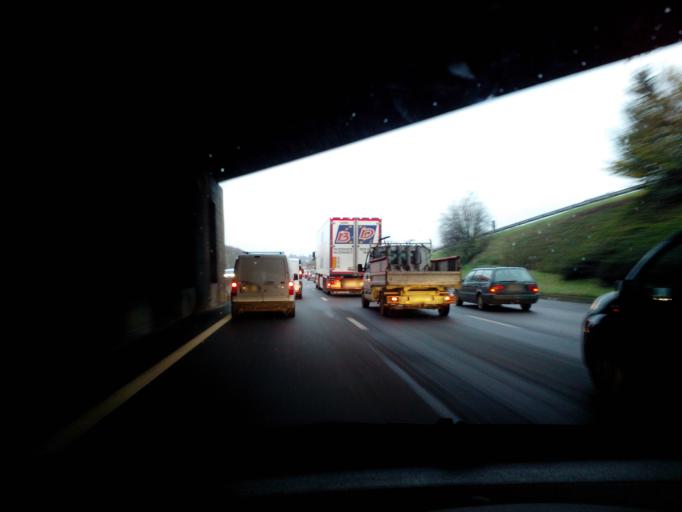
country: FR
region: Ile-de-France
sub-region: Departement de l'Essonne
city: Longjumeau
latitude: 48.6997
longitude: 2.3117
